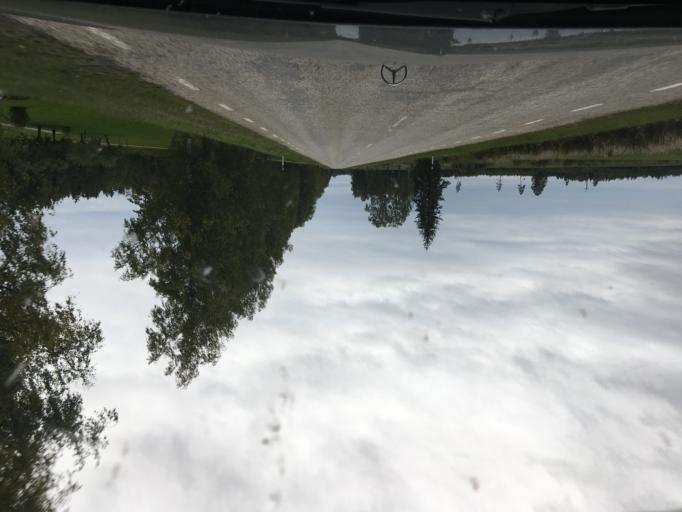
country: LV
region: Aluksnes Rajons
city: Aluksne
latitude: 57.5996
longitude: 27.1650
